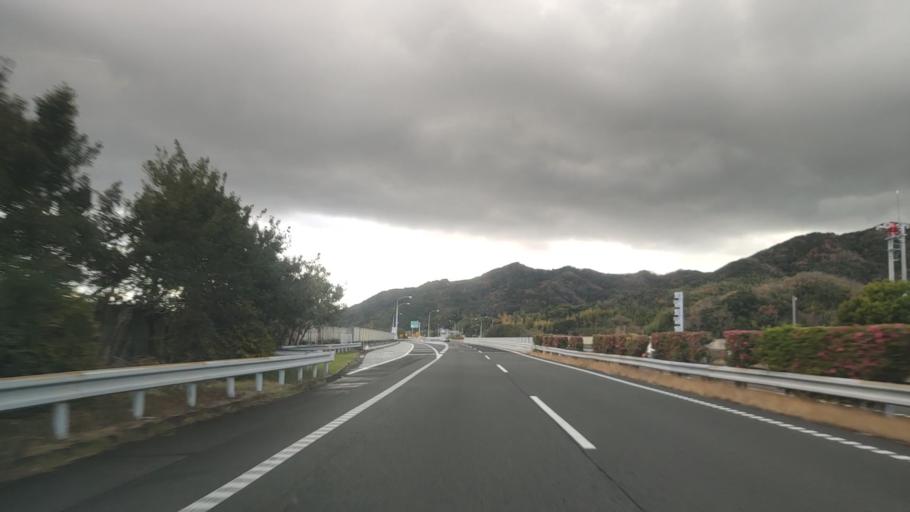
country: JP
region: Hyogo
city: Sumoto
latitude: 34.3440
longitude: 134.8497
